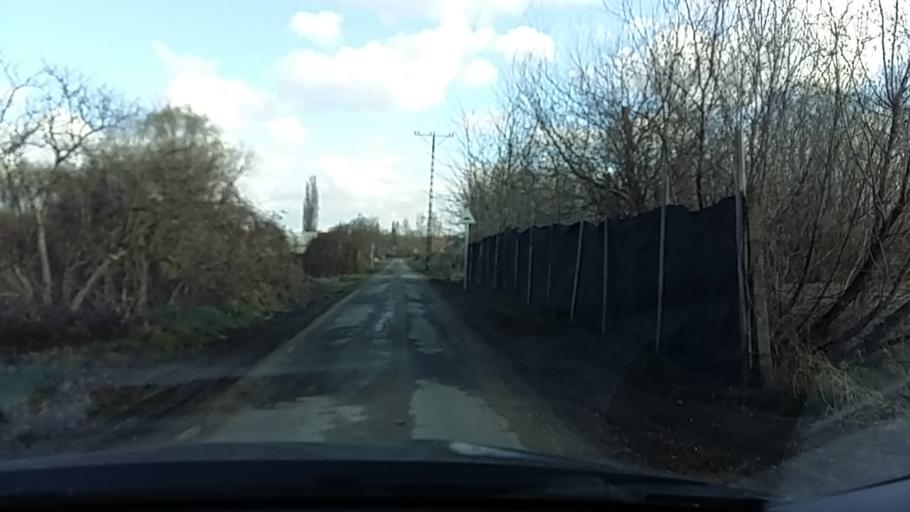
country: HU
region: Veszprem
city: Tapolca
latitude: 46.8744
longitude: 17.4382
